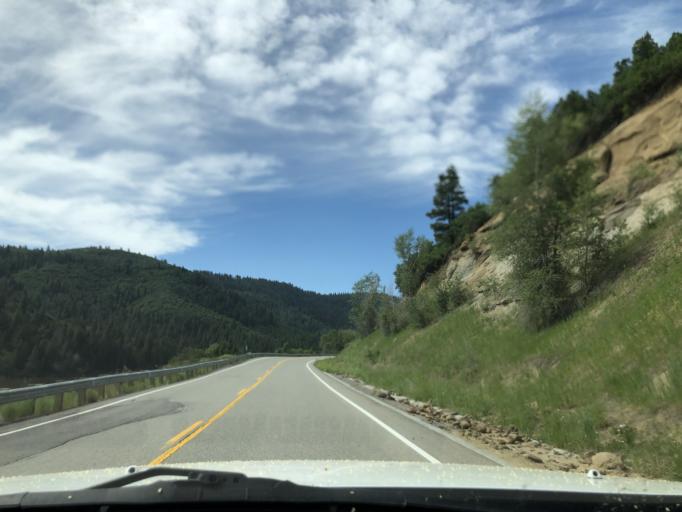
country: US
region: Colorado
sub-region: Delta County
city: Paonia
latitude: 38.9621
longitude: -107.3387
